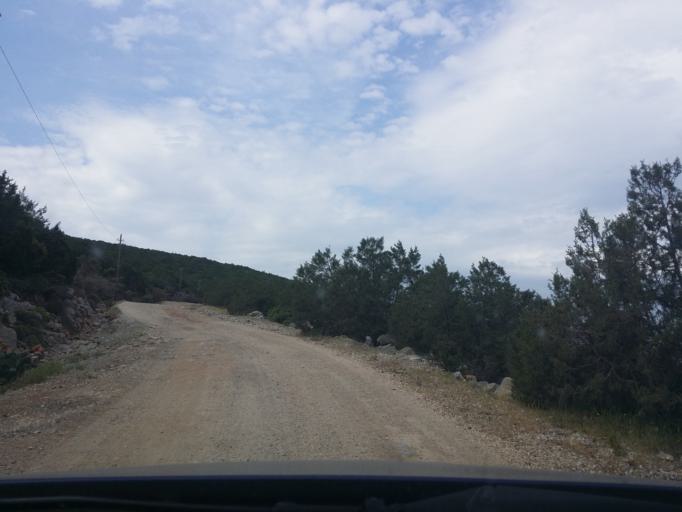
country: GR
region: Attica
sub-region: Nomos Piraios
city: Poros
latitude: 37.5327
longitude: 23.4755
